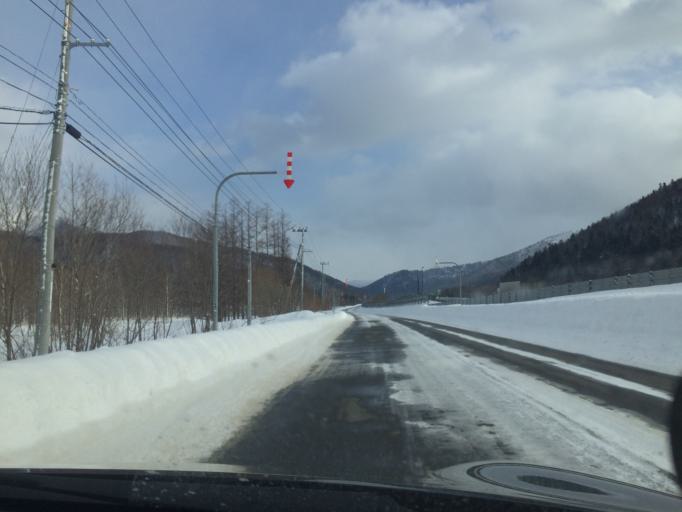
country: JP
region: Hokkaido
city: Shimo-furano
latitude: 43.0651
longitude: 142.5401
